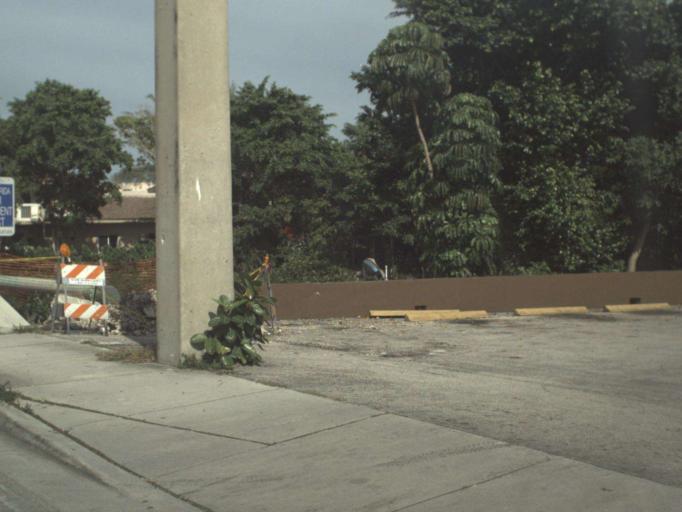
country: US
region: Florida
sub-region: Miami-Dade County
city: North Miami
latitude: 25.8861
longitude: -80.1913
